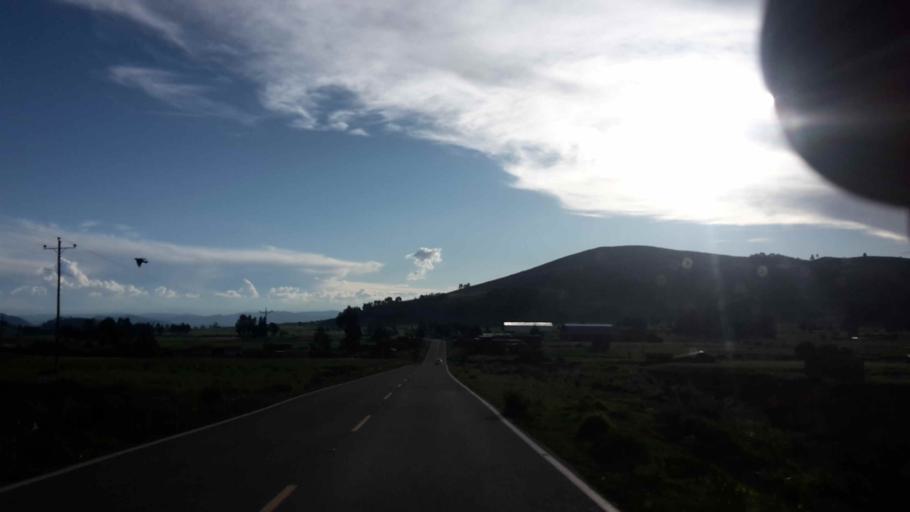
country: BO
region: Cochabamba
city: Arani
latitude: -17.5485
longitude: -65.6808
